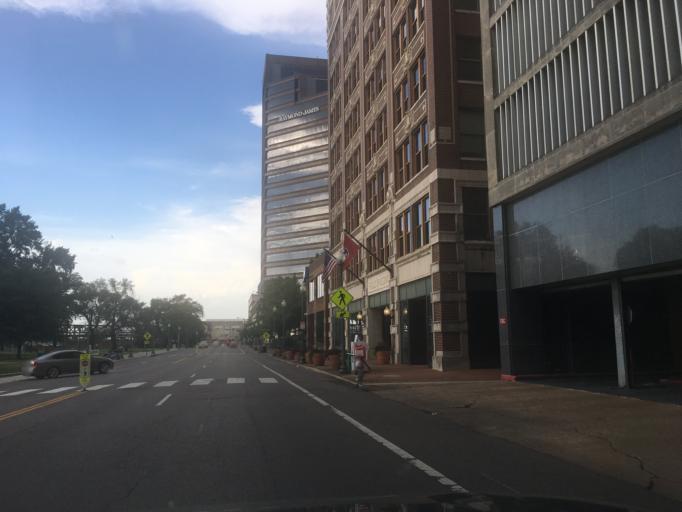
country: US
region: Tennessee
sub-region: Shelby County
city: Memphis
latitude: 35.1458
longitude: -90.0539
